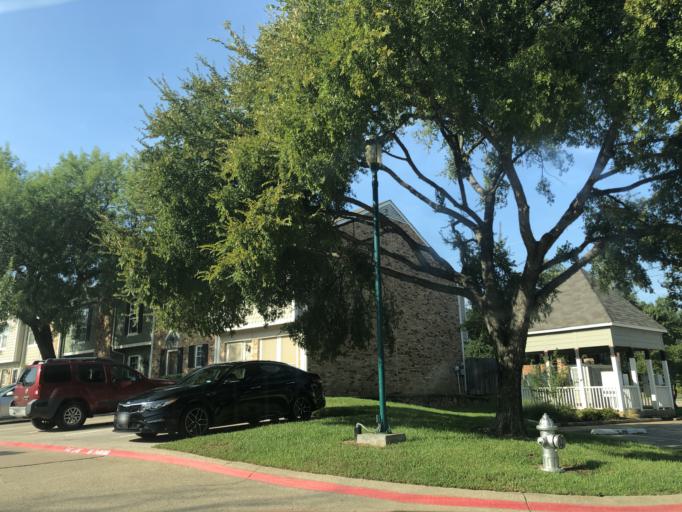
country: US
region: Texas
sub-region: Tarrant County
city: Euless
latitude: 32.8675
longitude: -97.0824
